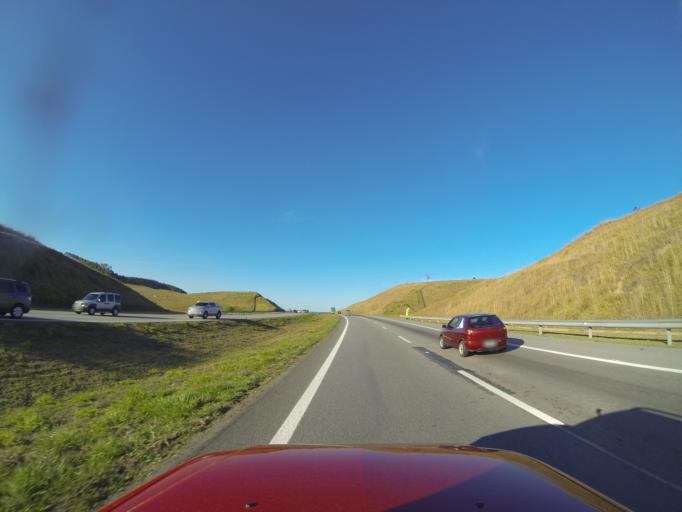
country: BR
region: Sao Paulo
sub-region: Jacarei
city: Jacarei
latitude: -23.3371
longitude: -45.9388
